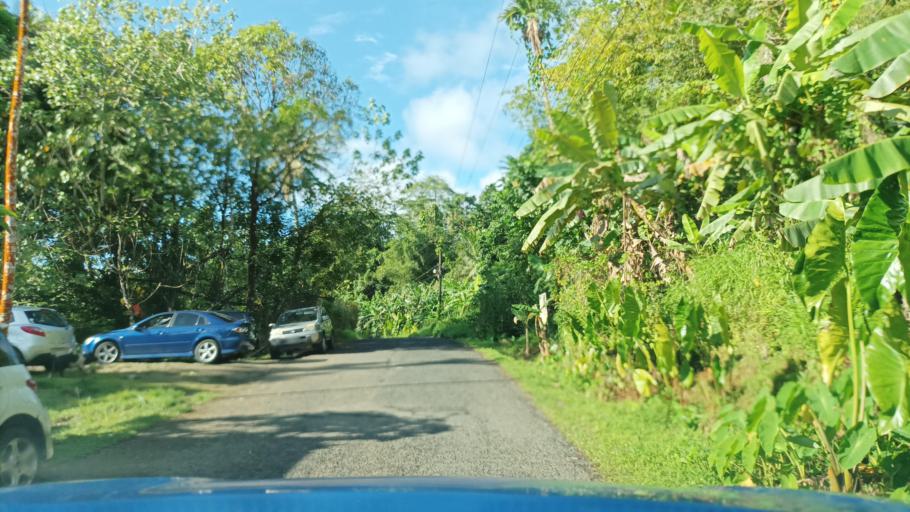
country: FM
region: Pohnpei
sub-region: Kolonia Municipality
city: Kolonia Town
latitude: 6.9596
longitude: 158.1853
